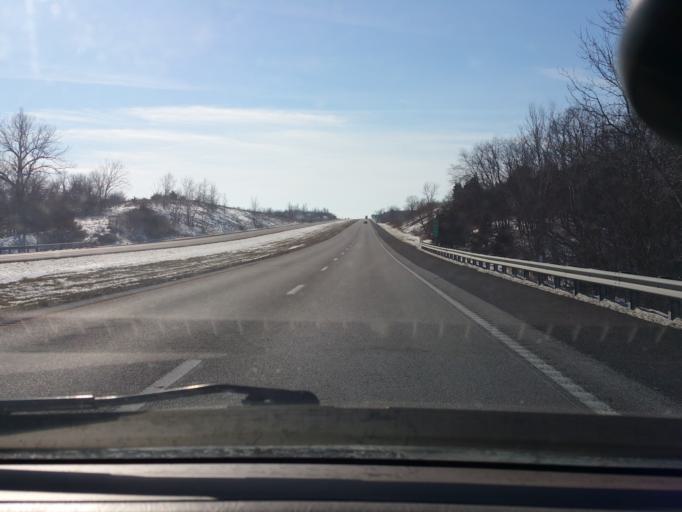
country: US
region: Missouri
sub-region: Daviess County
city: Gallatin
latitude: 39.9145
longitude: -94.1437
